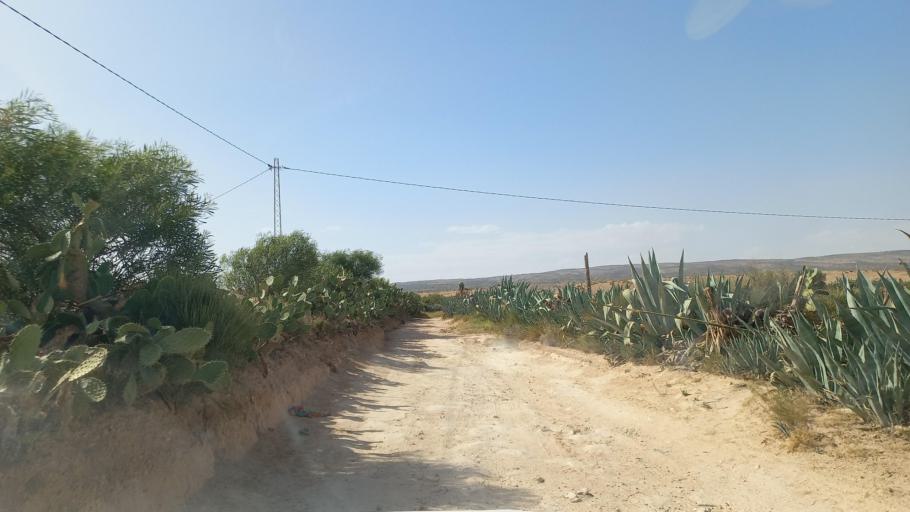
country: TN
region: Al Qasrayn
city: Kasserine
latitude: 35.2780
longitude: 8.9400
